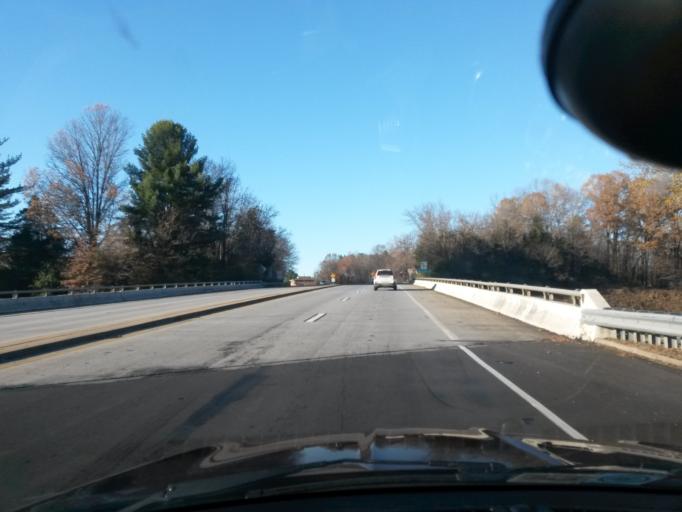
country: US
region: Virginia
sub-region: Amherst County
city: Amherst
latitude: 37.5811
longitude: -79.0459
